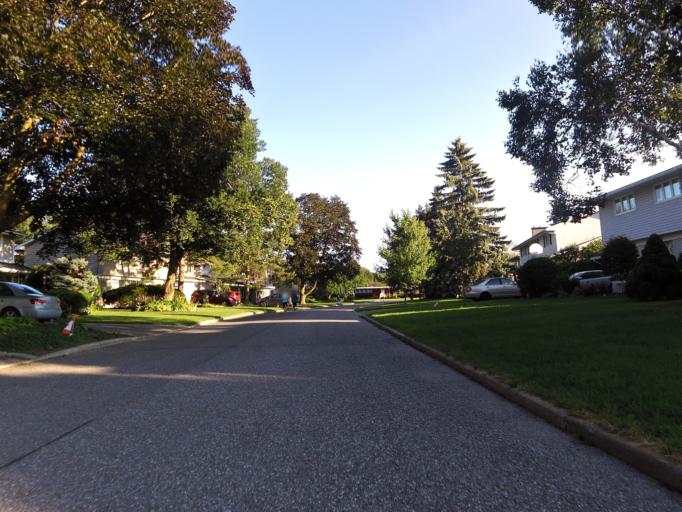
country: CA
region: Ontario
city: Bells Corners
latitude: 45.3430
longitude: -75.8036
